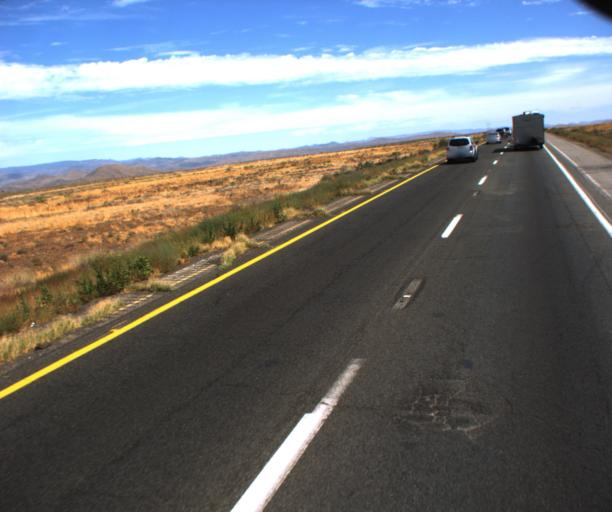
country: US
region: Arizona
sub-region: Yavapai County
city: Black Canyon City
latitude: 34.1639
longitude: -112.1375
